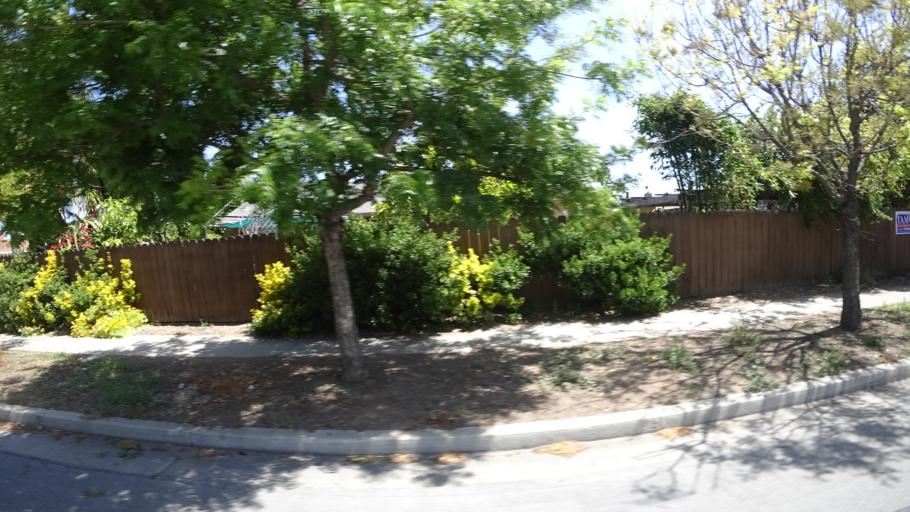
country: US
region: California
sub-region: Santa Clara County
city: Seven Trees
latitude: 37.3179
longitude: -121.8391
